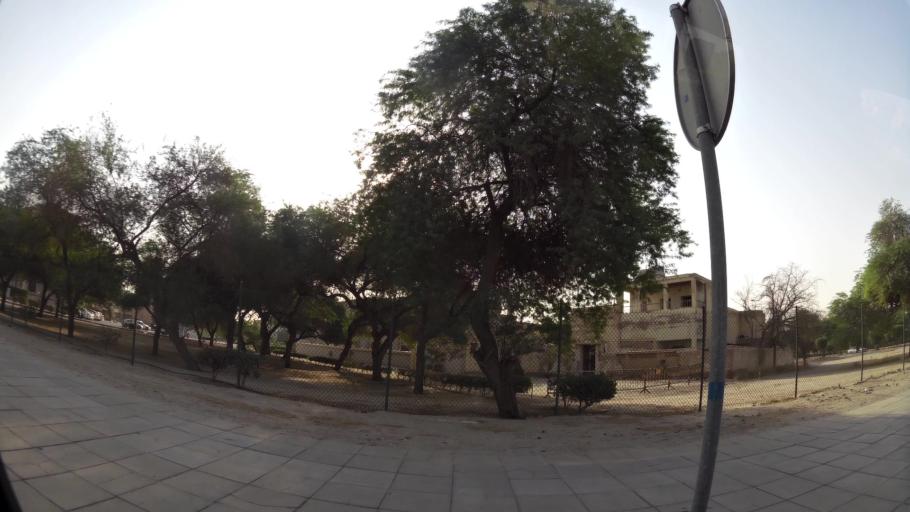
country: KW
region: Al Asimah
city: Ad Dasmah
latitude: 29.3635
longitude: 47.9955
